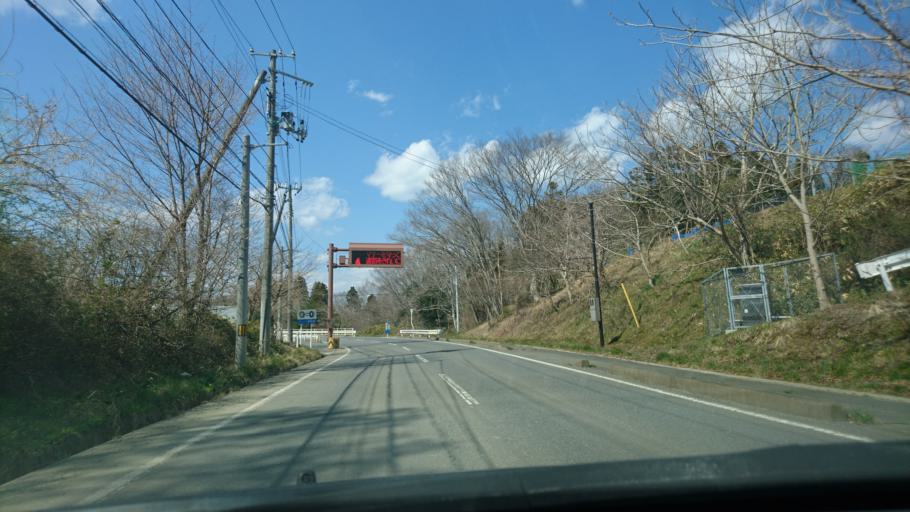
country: JP
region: Miyagi
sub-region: Oshika Gun
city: Onagawa Cho
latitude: 38.6385
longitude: 141.4988
